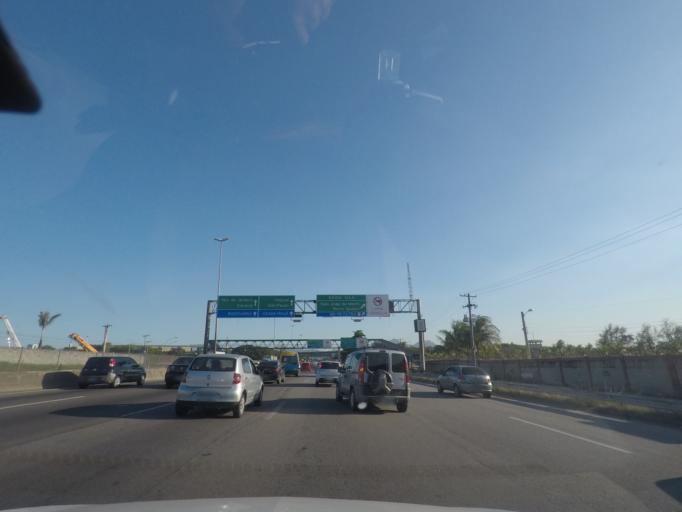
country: BR
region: Rio de Janeiro
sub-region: Duque De Caxias
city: Duque de Caxias
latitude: -22.8051
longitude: -43.2898
